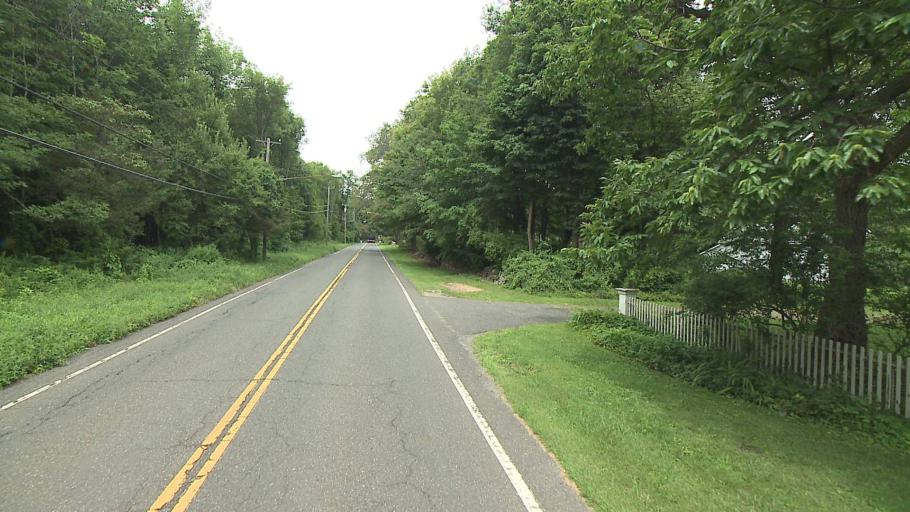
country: US
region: Connecticut
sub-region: Litchfield County
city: New Milford
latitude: 41.5249
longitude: -73.3648
